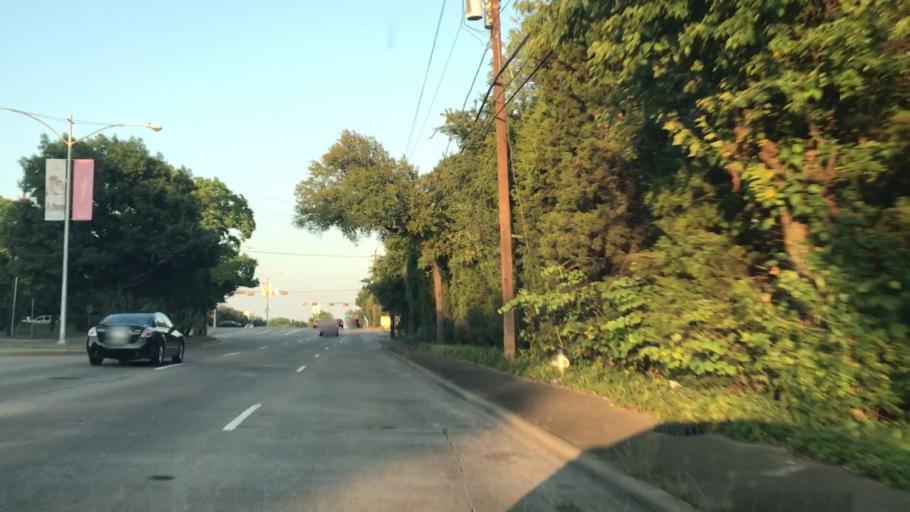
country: US
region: Texas
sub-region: Dallas County
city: University Park
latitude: 32.9096
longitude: -96.7885
